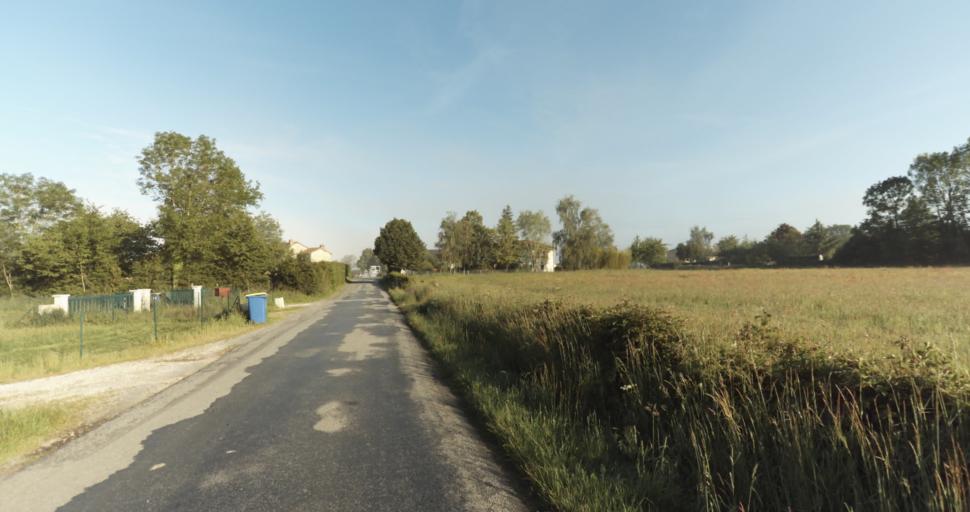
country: FR
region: Limousin
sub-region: Departement de la Haute-Vienne
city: Condat-sur-Vienne
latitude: 45.7823
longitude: 1.2847
